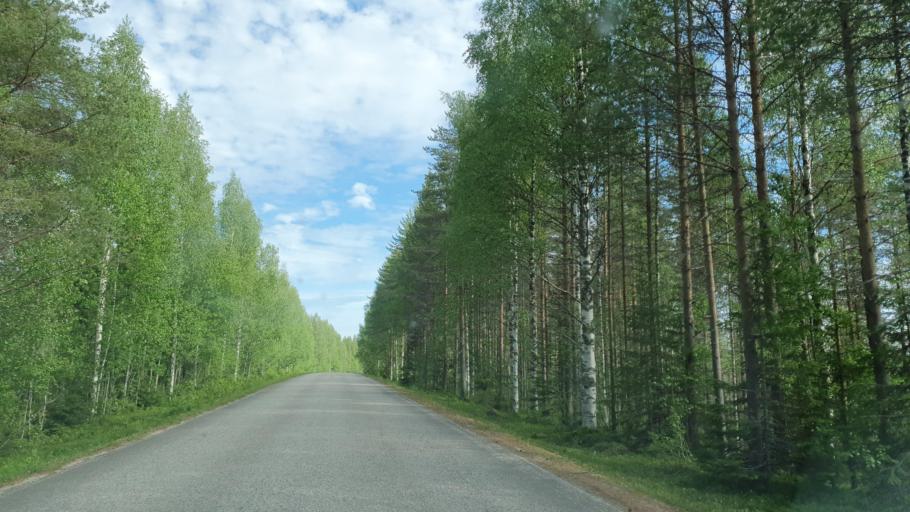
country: FI
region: Kainuu
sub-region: Kehys-Kainuu
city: Kuhmo
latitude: 64.5278
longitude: 29.3672
